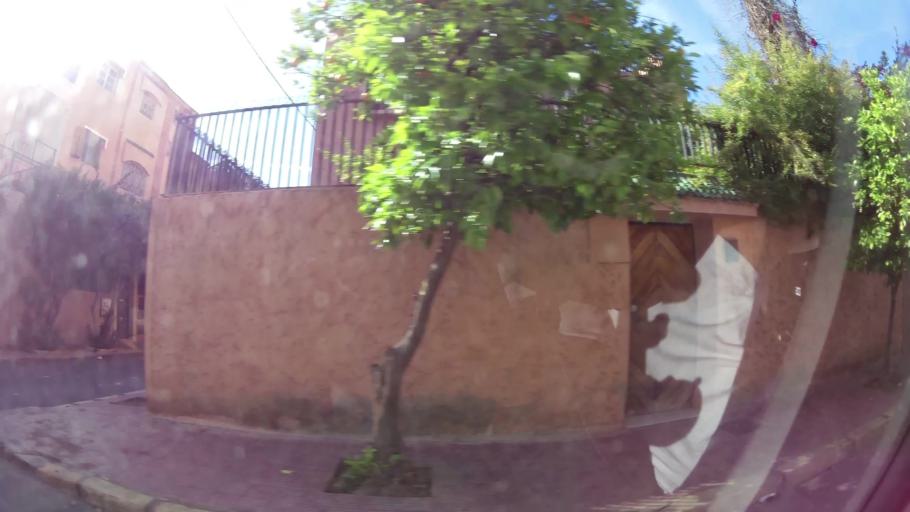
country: MA
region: Marrakech-Tensift-Al Haouz
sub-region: Marrakech
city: Marrakesh
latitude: 31.6440
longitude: -8.0073
